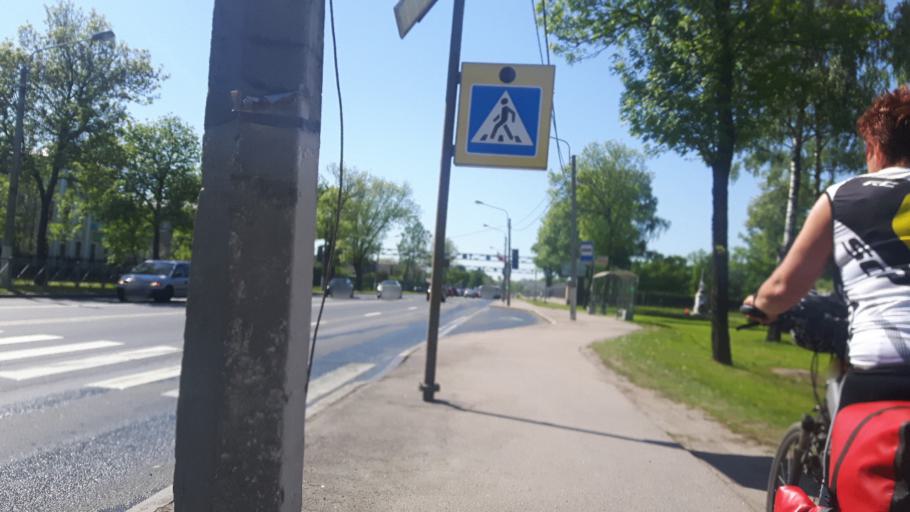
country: RU
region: St.-Petersburg
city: Strel'na
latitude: 59.8518
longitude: 30.0702
